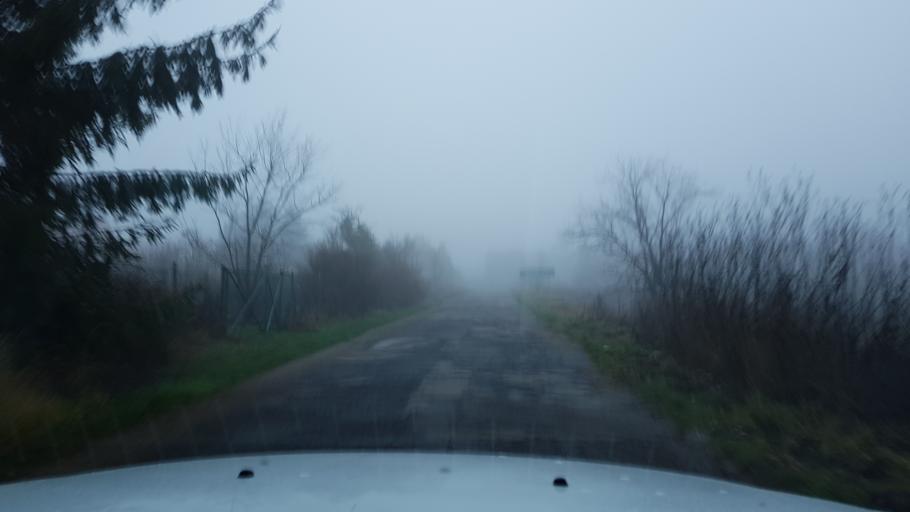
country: PL
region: West Pomeranian Voivodeship
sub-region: Powiat mysliborski
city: Mysliborz
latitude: 52.9464
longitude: 14.7918
